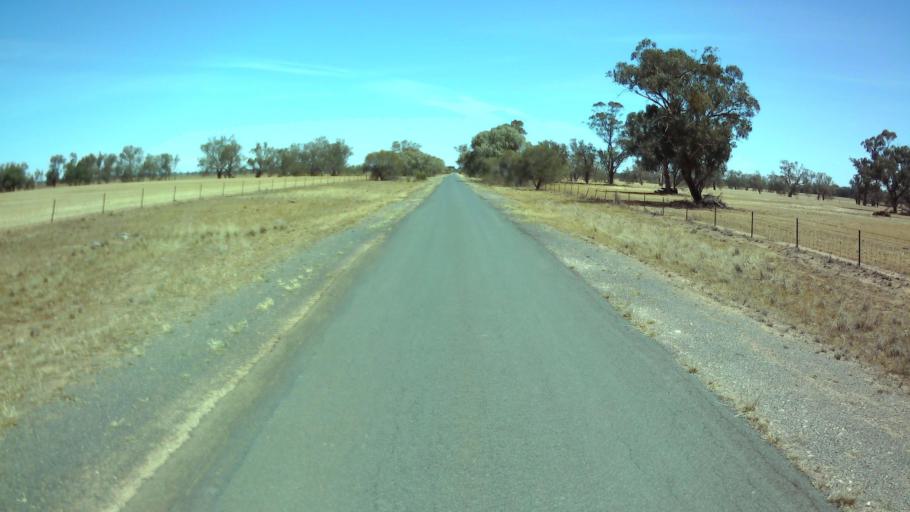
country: AU
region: New South Wales
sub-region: Weddin
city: Grenfell
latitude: -33.8465
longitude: 147.6964
